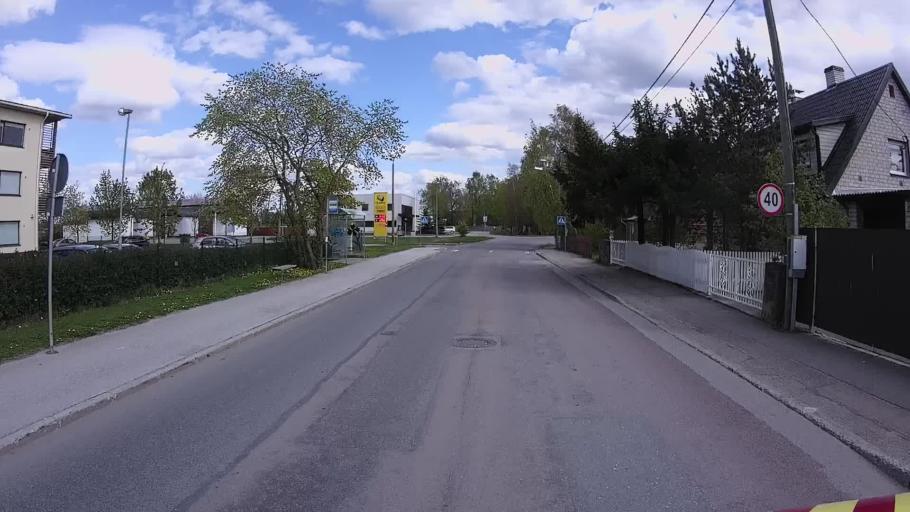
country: EE
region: Tartu
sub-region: Tartu linn
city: Tartu
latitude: 58.4010
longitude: 26.7266
